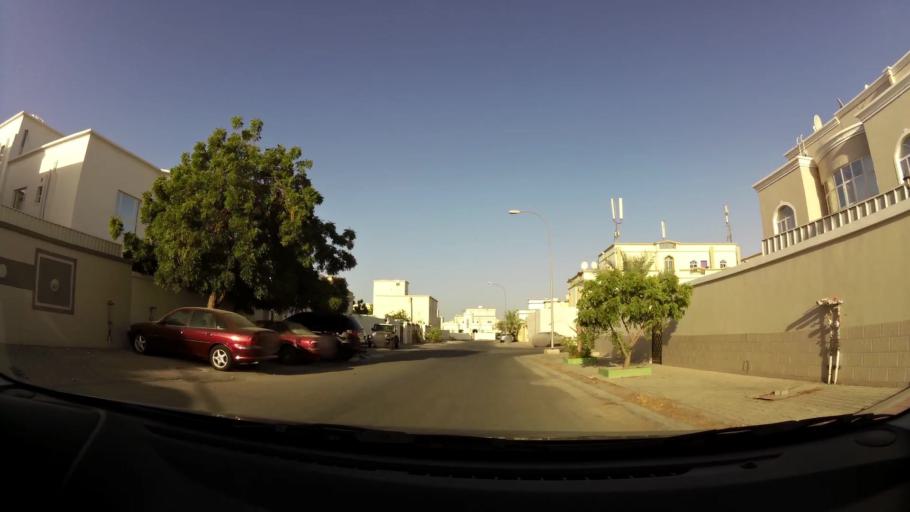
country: OM
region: Muhafazat Masqat
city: As Sib al Jadidah
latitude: 23.6124
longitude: 58.2233
